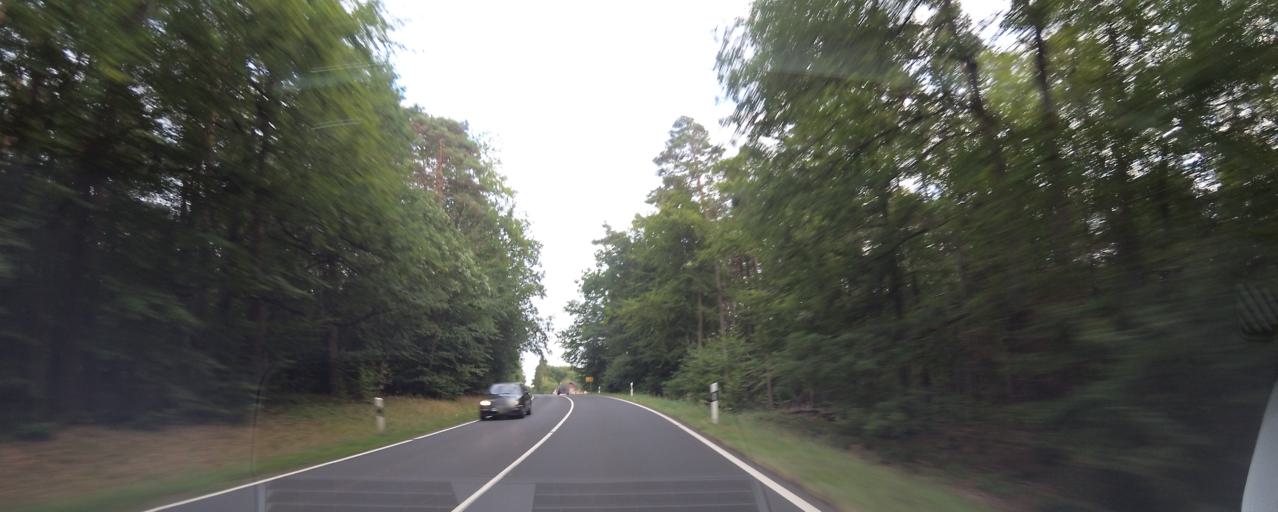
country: DE
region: Rheinland-Pfalz
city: Zemmer
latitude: 49.9097
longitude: 6.7071
